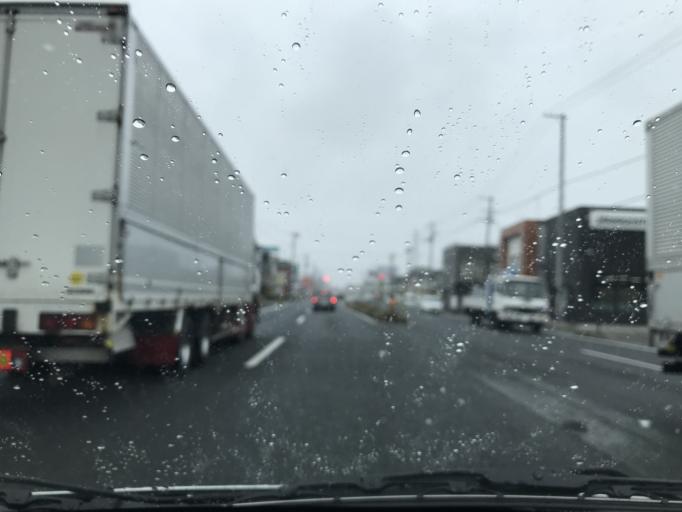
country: JP
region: Iwate
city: Kitakami
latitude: 39.2895
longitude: 141.1044
